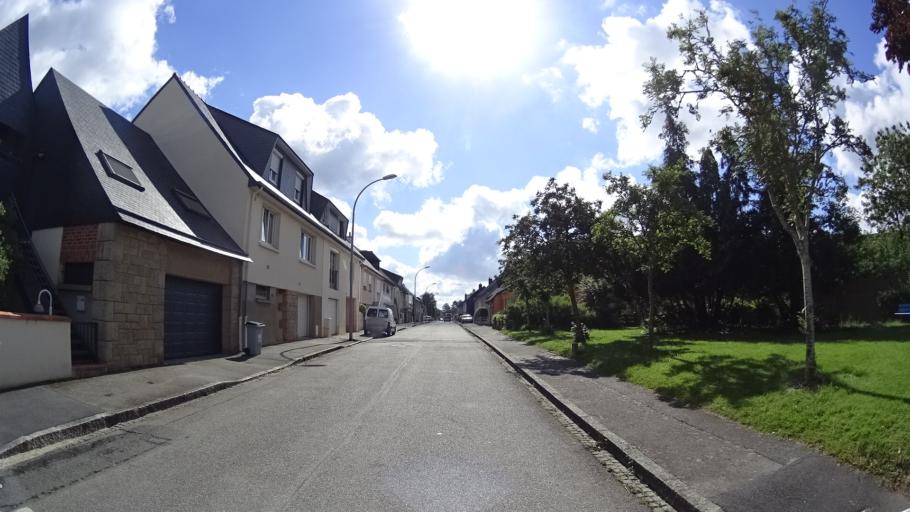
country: FR
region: Brittany
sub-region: Departement d'Ille-et-Vilaine
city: Saint-Gilles
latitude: 48.1284
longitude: -1.8184
